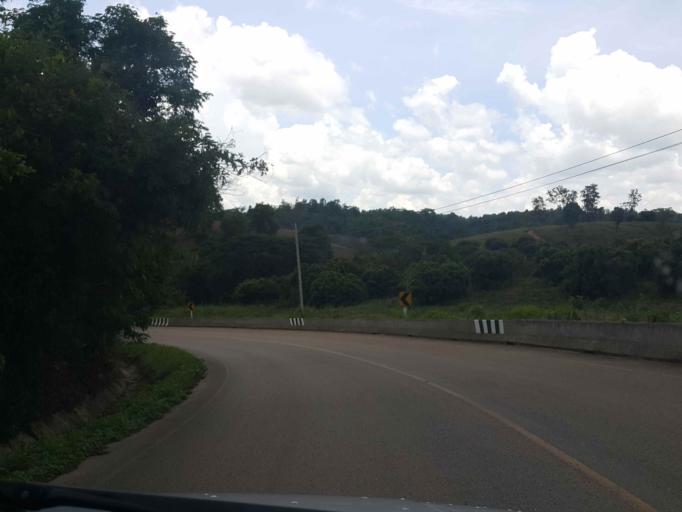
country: TH
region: Lampang
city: Ngao
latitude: 18.9421
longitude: 100.0766
